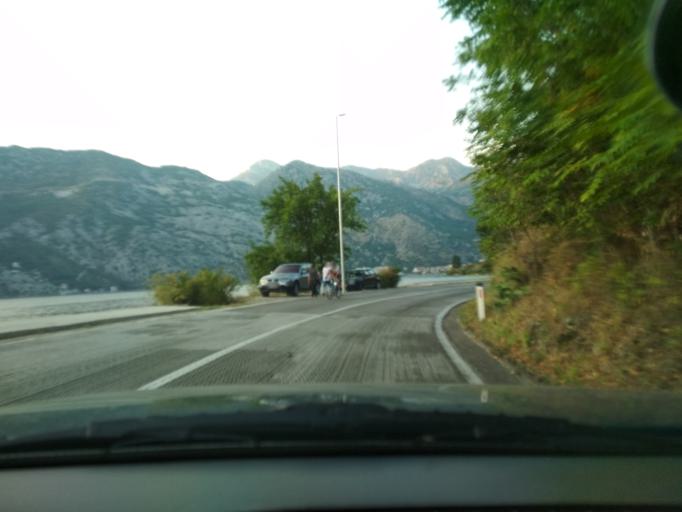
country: ME
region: Kotor
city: Risan
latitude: 42.5018
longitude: 18.6922
